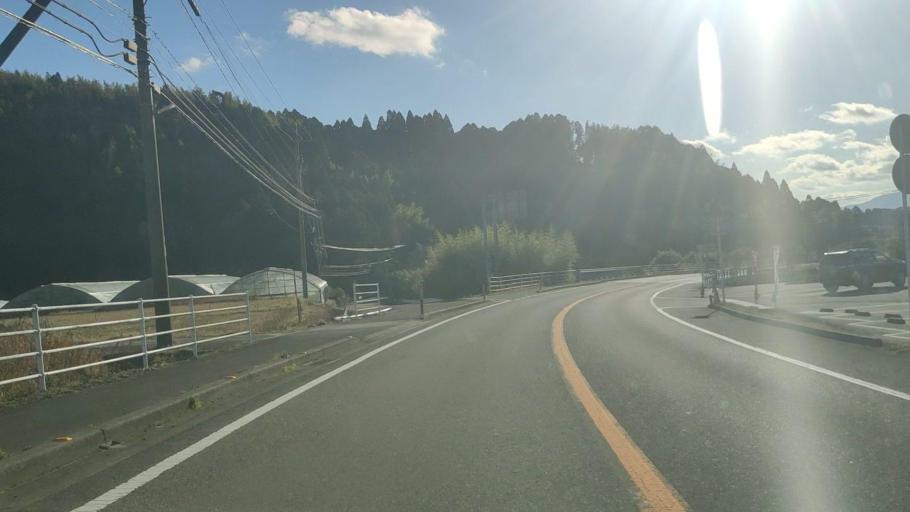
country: JP
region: Fukuoka
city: Maebaru-chuo
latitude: 33.4506
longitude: 130.2757
